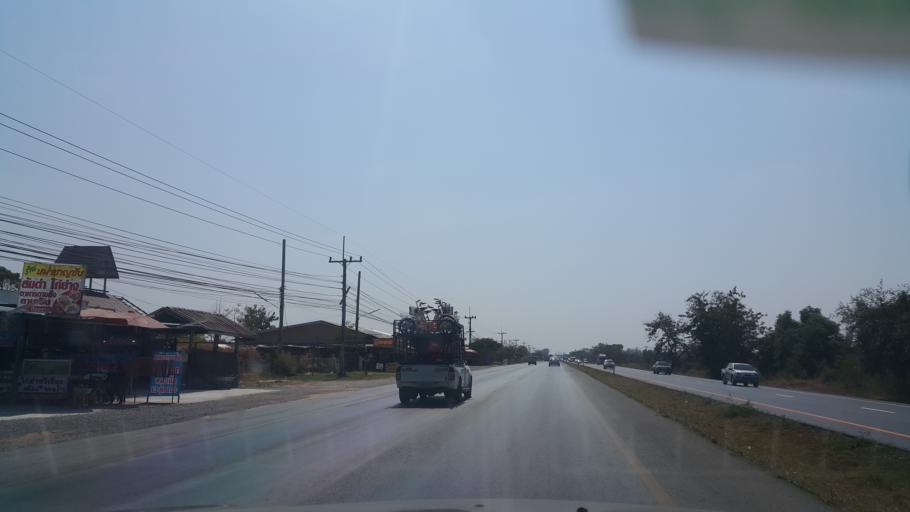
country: TH
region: Khon Kaen
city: Non Sila
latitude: 15.9925
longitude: 102.6998
